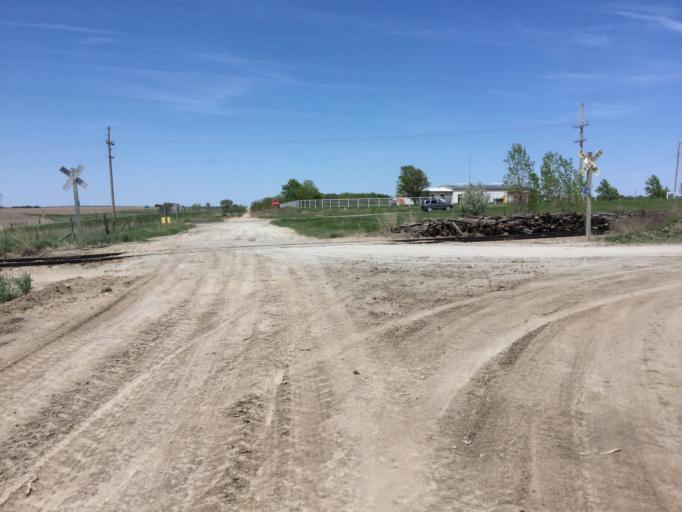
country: US
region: Kansas
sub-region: Smith County
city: Smith Center
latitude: 39.7699
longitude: -98.8045
